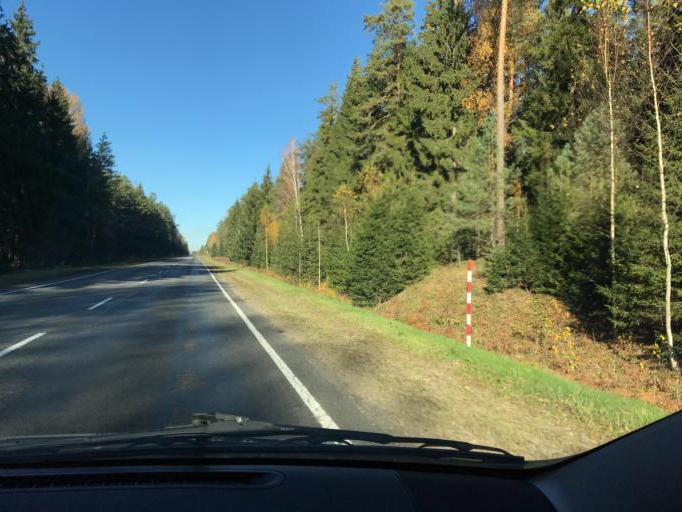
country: BY
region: Vitebsk
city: Polatsk
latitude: 55.4061
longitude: 28.8042
